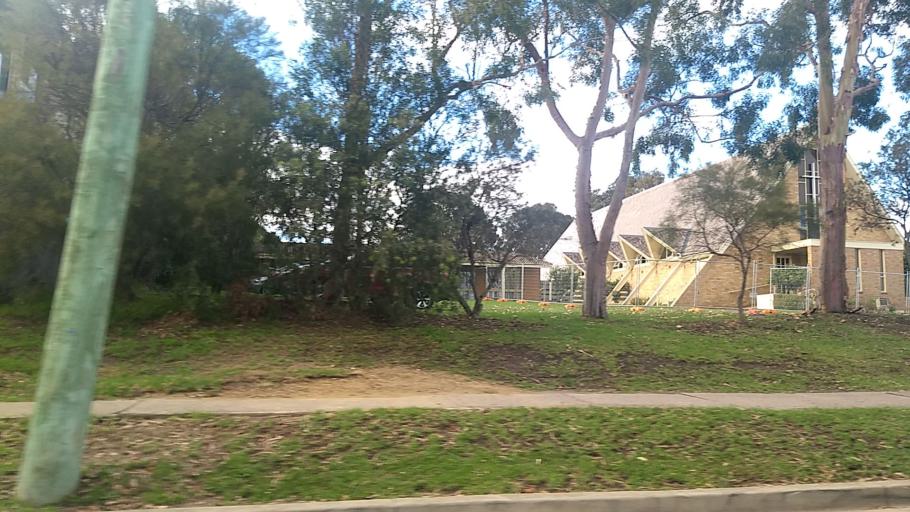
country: AU
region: New South Wales
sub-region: Bega Valley
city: Merimbula
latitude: -36.8866
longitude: 149.9126
